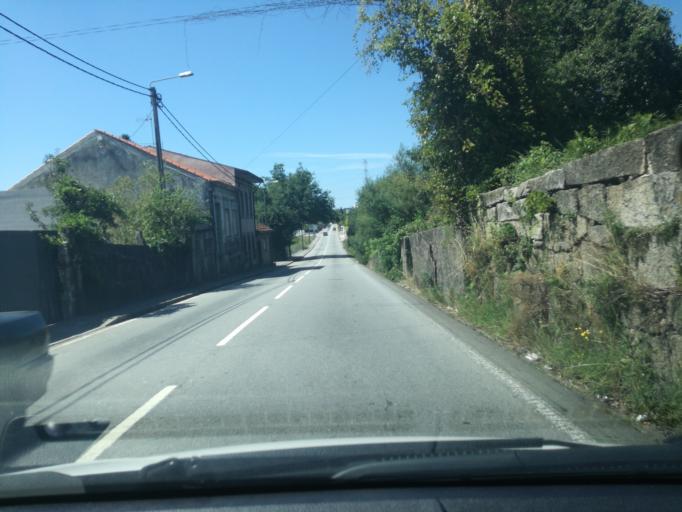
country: PT
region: Porto
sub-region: Maia
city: Nogueira
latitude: 41.2304
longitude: -8.5891
